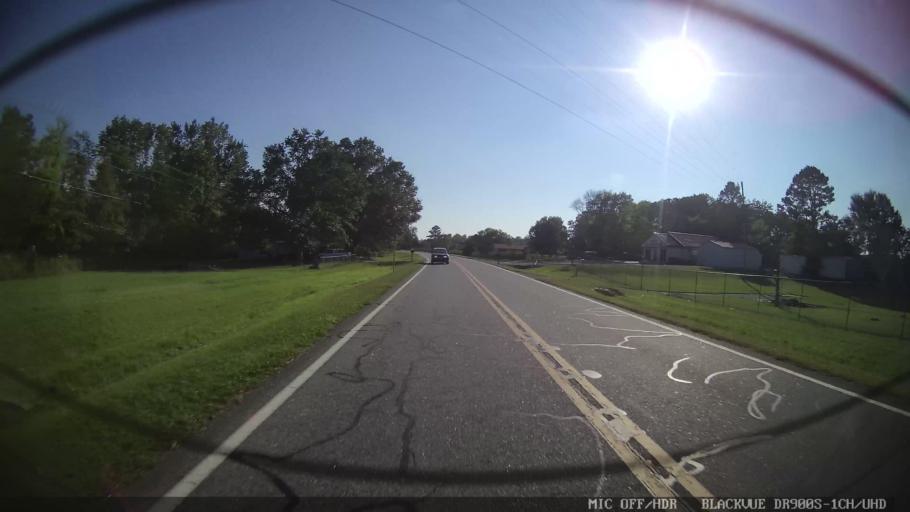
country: US
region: Georgia
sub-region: Gordon County
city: Calhoun
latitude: 34.5845
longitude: -84.8773
